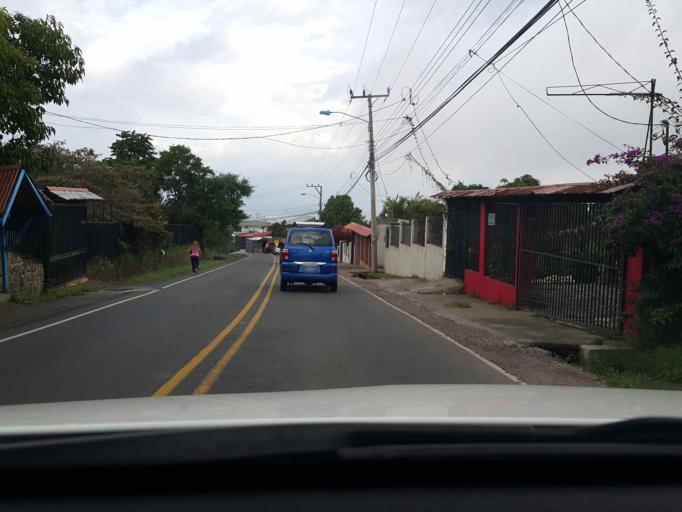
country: CR
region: Heredia
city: San Josecito
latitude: 10.0274
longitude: -84.0951
